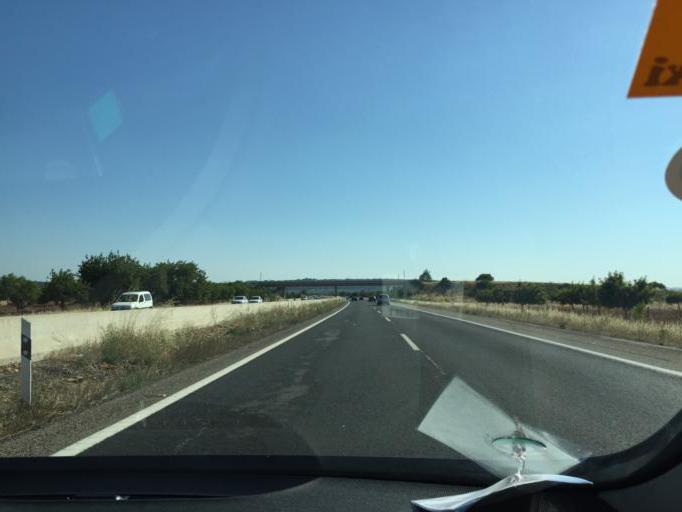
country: ES
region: Balearic Islands
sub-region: Illes Balears
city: Consell
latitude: 39.6582
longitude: 2.8054
